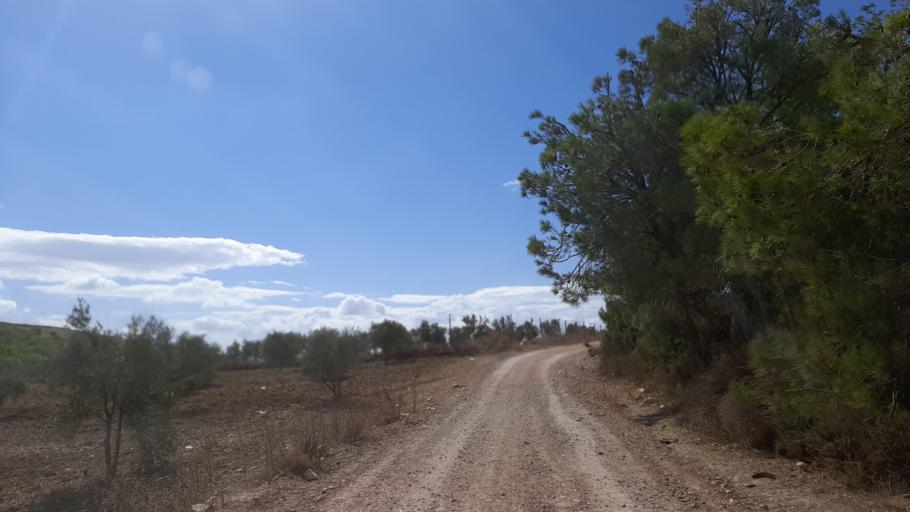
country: TN
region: Zaghwan
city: Zaghouan
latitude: 36.5121
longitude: 10.1835
